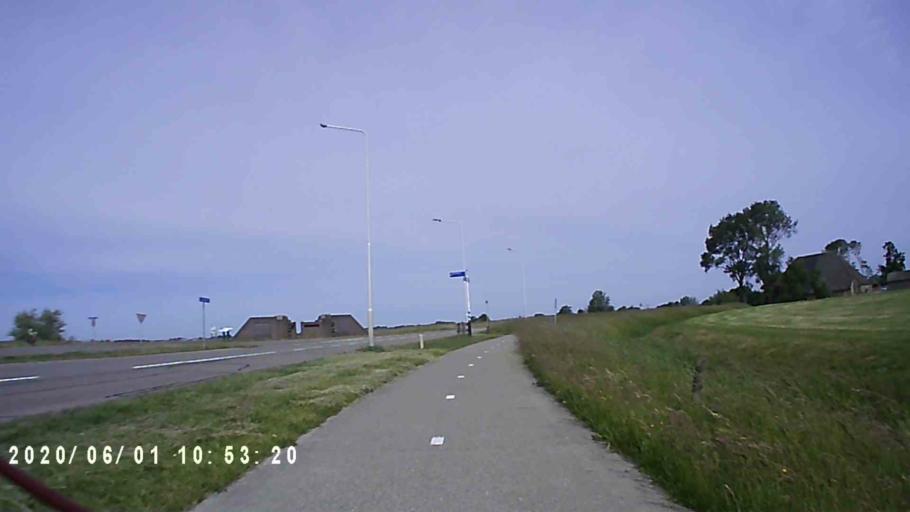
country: NL
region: Friesland
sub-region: Gemeente Franekeradeel
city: Franeker
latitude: 53.2017
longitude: 5.5138
